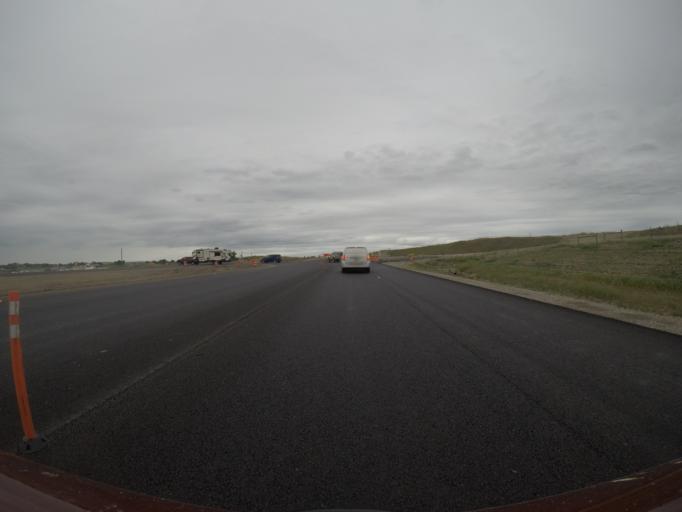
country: US
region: Montana
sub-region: Yellowstone County
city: Laurel
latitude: 45.6409
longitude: -108.7658
